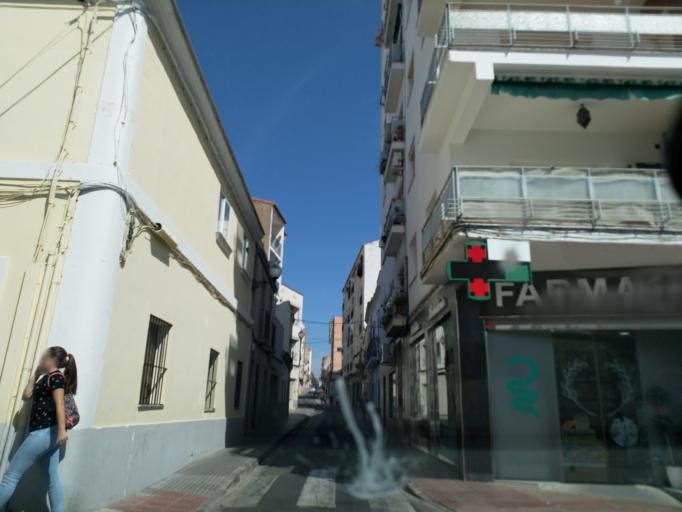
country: ES
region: Extremadura
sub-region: Provincia de Badajoz
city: Merida
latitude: 38.9145
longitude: -6.3433
